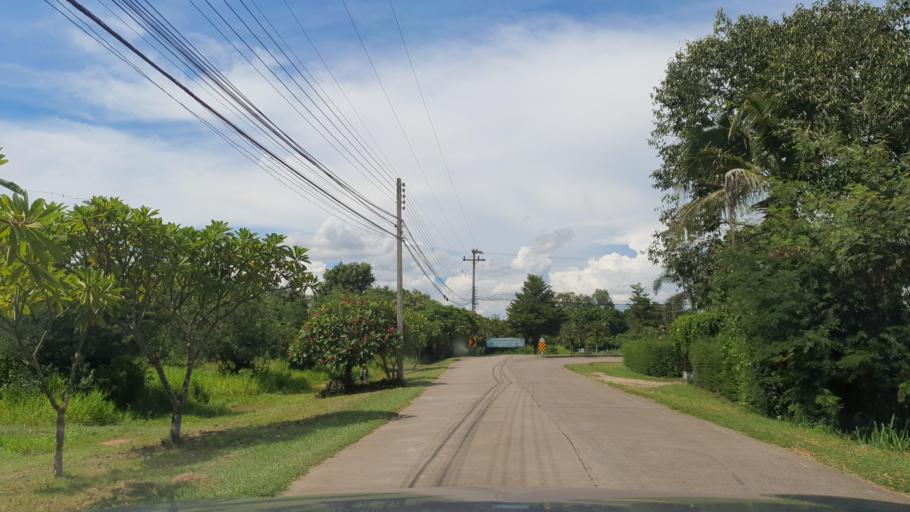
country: TH
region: Chiang Mai
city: San Pa Tong
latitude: 18.5894
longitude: 98.8740
